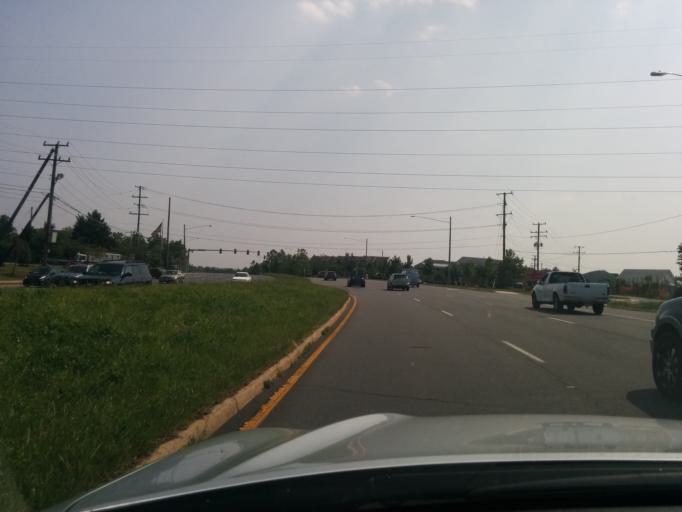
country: US
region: Virginia
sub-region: Fairfax County
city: Floris
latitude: 38.9496
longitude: -77.4124
